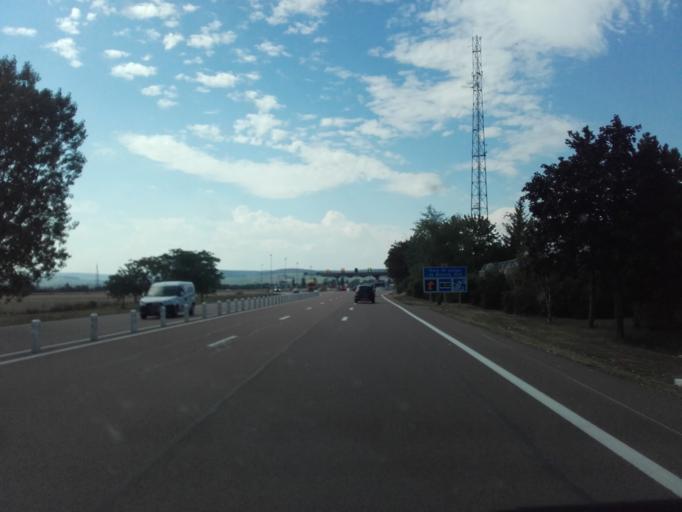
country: FR
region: Bourgogne
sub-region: Departement de la Cote-d'Or
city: Bligny-les-Beaune
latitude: 47.0012
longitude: 4.8575
